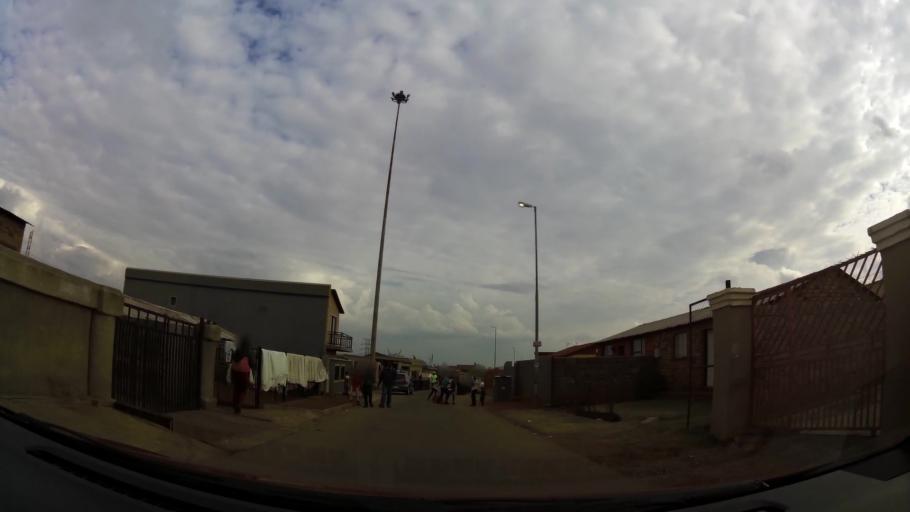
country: ZA
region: Gauteng
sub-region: City of Johannesburg Metropolitan Municipality
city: Soweto
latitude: -26.2454
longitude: 27.8389
